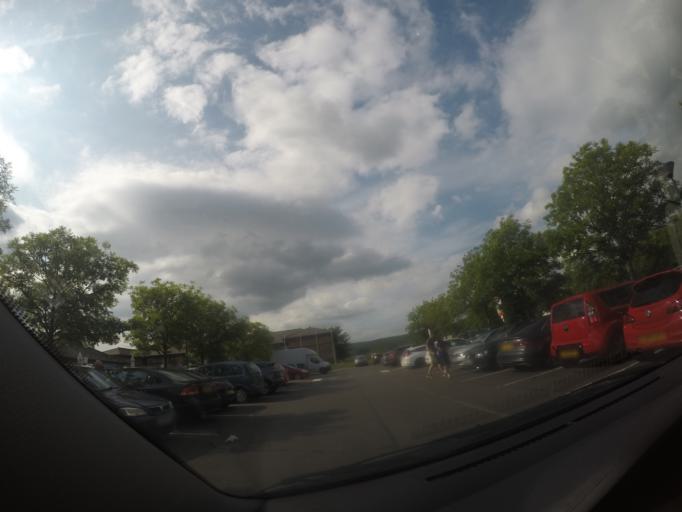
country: GB
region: Scotland
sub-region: South Lanarkshire
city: Douglas
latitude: 55.5074
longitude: -3.6950
